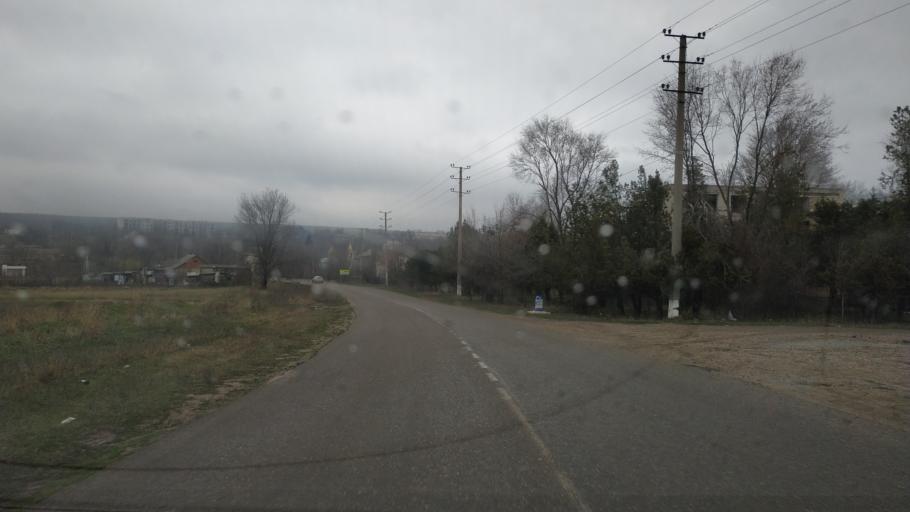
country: MD
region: Cantemir
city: Visniovca
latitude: 46.3332
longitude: 28.4538
